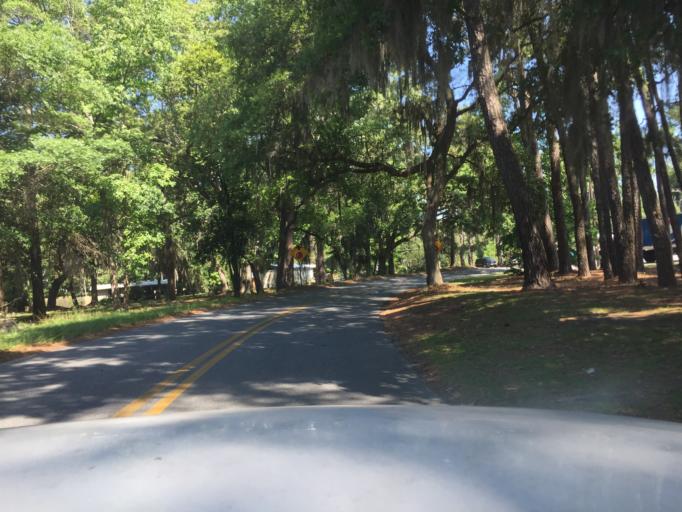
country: US
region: Georgia
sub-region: Chatham County
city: Montgomery
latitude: 31.9458
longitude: -81.1134
